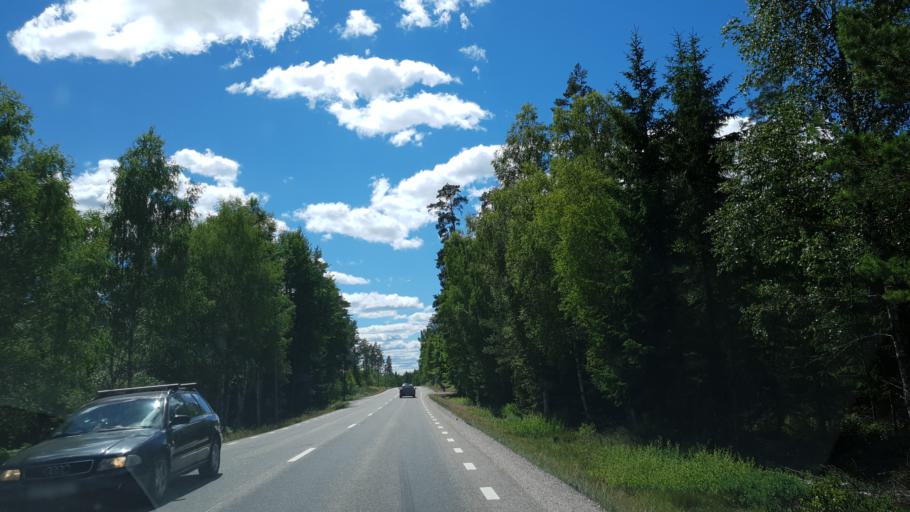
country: SE
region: Kronoberg
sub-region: Lessebo Kommun
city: Lessebo
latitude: 56.8226
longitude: 15.3835
